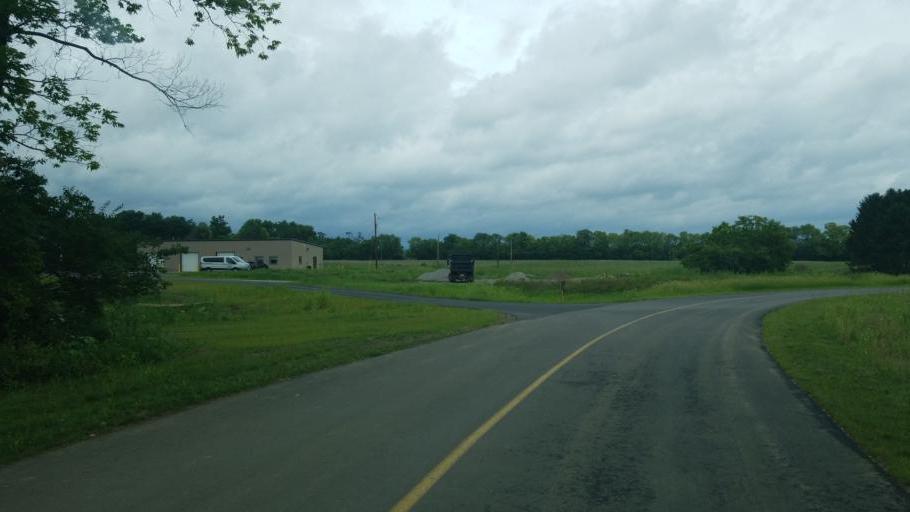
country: US
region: Ohio
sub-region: Franklin County
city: Grove City
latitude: 39.8491
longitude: -83.0260
